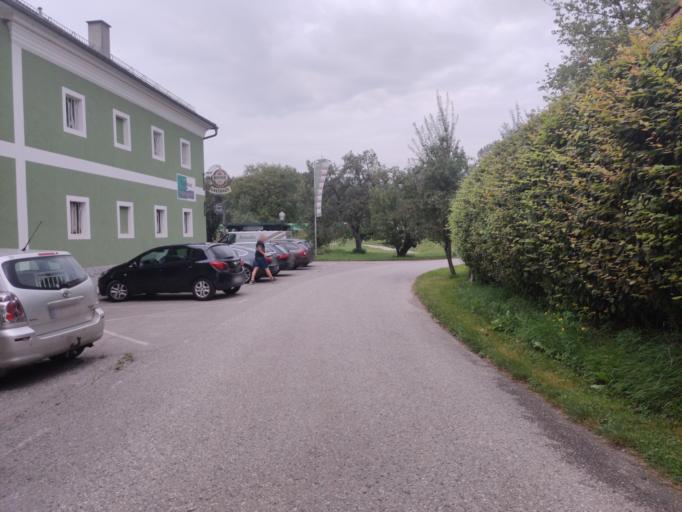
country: AT
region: Lower Austria
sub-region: Politischer Bezirk Amstetten
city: Ennsdorf
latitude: 48.2327
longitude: 14.5262
